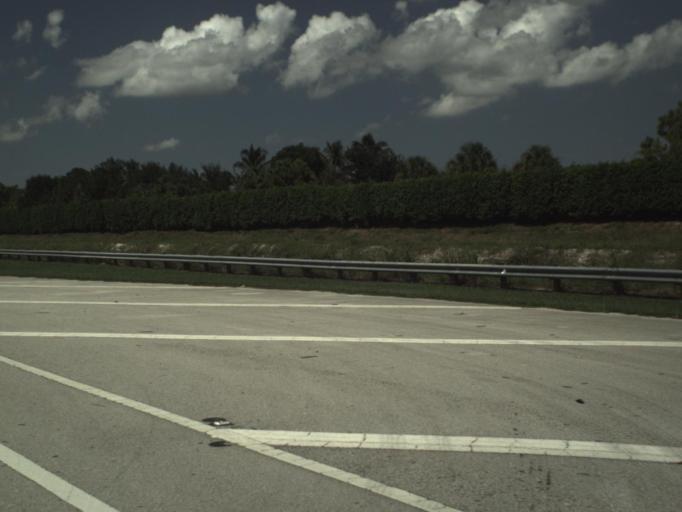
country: US
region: Florida
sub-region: Palm Beach County
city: Wellington
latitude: 26.6022
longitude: -80.2053
